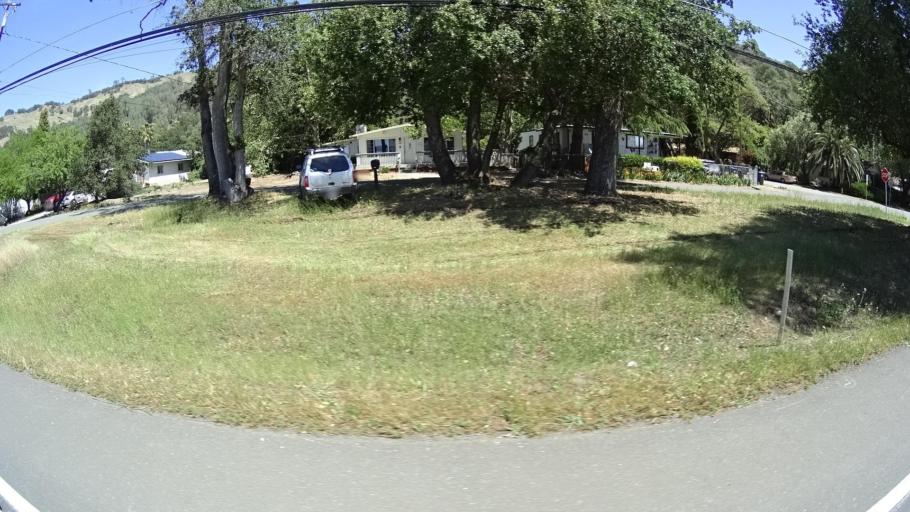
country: US
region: California
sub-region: Lake County
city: Lucerne
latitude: 39.0740
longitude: -122.7826
